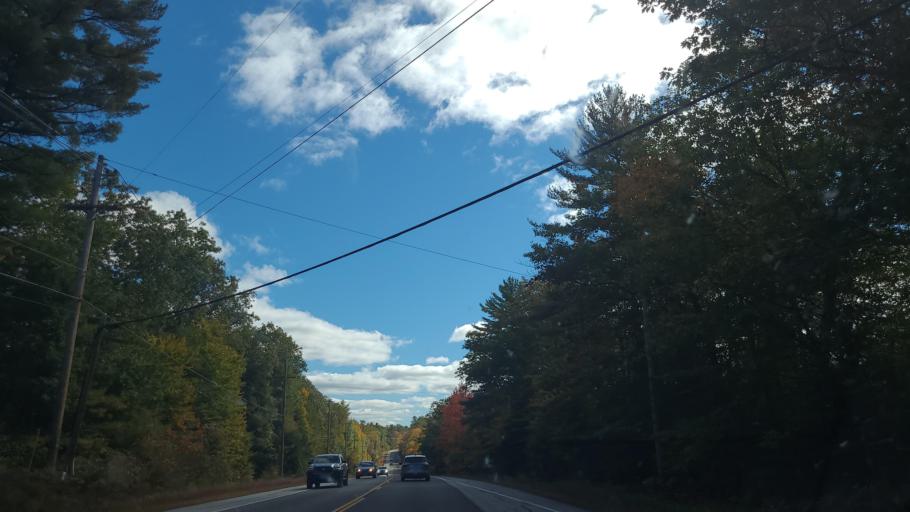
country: US
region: Maine
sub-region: Cumberland County
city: Bridgton
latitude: 43.9871
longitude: -70.6446
